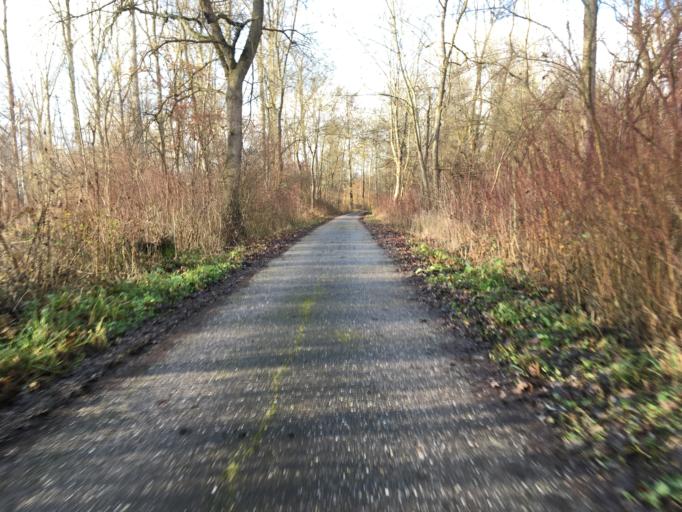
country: DE
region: Baden-Wuerttemberg
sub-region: Karlsruhe Region
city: Philippsburg
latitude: 49.2477
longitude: 8.4280
